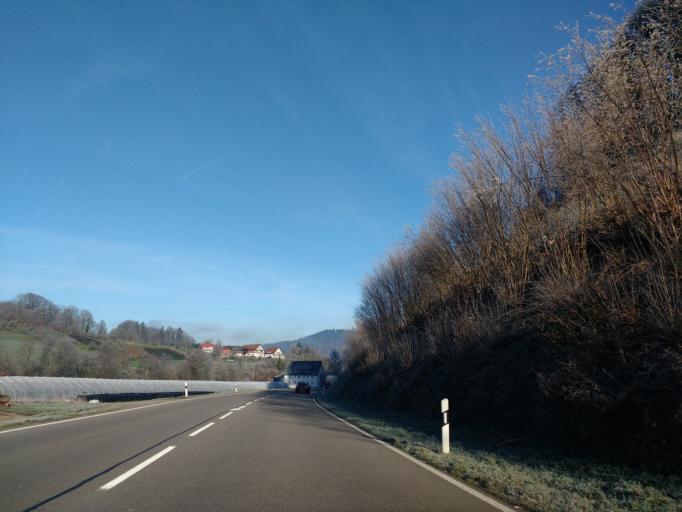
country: DE
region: Baden-Wuerttemberg
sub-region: Freiburg Region
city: Oppenau
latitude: 48.4620
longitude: 8.1614
